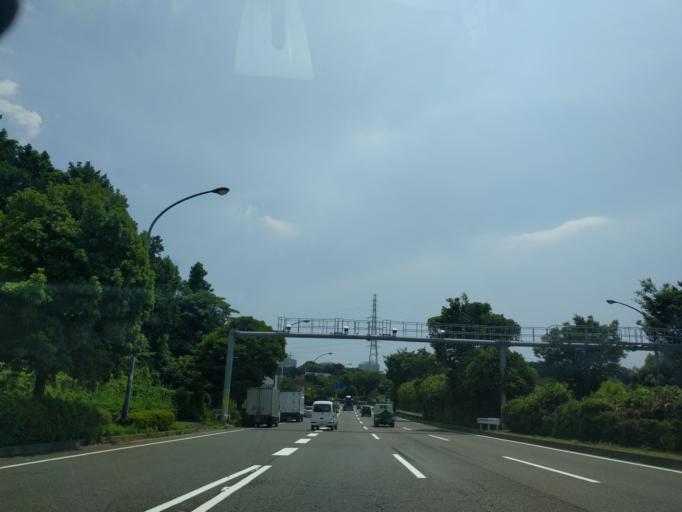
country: JP
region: Kanagawa
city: Yokohama
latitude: 35.4403
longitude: 139.5604
